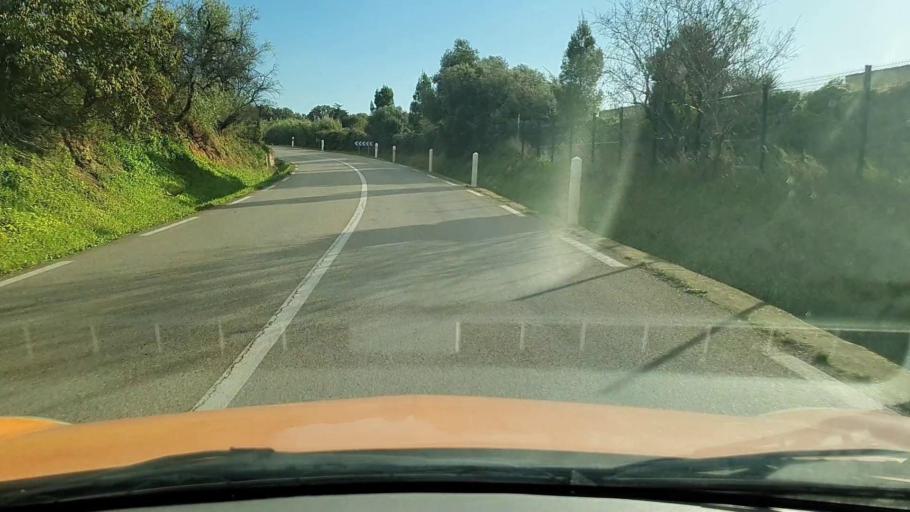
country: FR
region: Languedoc-Roussillon
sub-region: Departement du Gard
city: Vauvert
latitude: 43.6843
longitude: 4.2737
